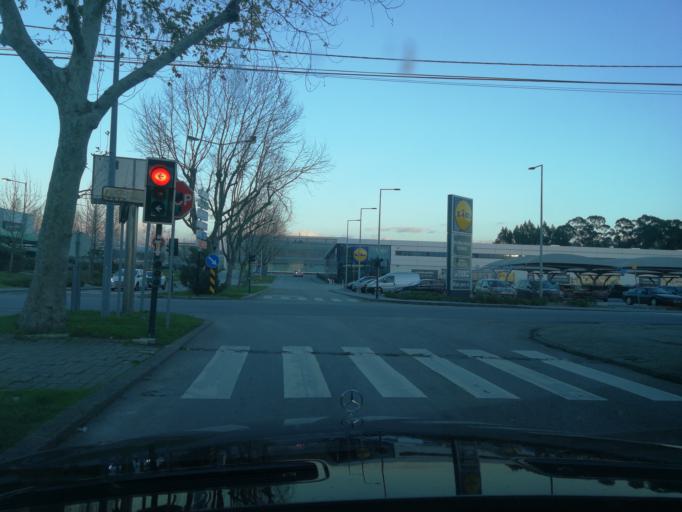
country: PT
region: Aveiro
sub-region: Estarreja
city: Estarreja
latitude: 40.7617
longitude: -8.5714
